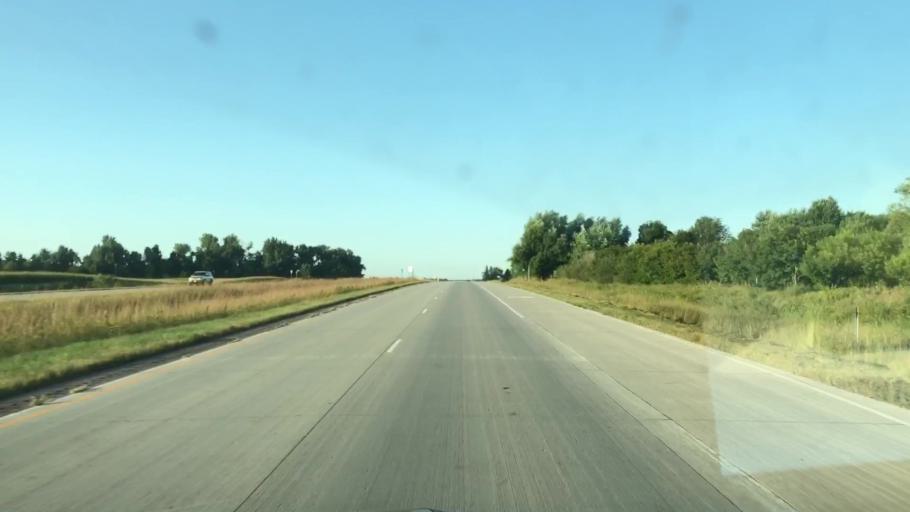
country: US
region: Minnesota
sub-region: Nobles County
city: Worthington
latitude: 43.5823
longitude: -95.6493
